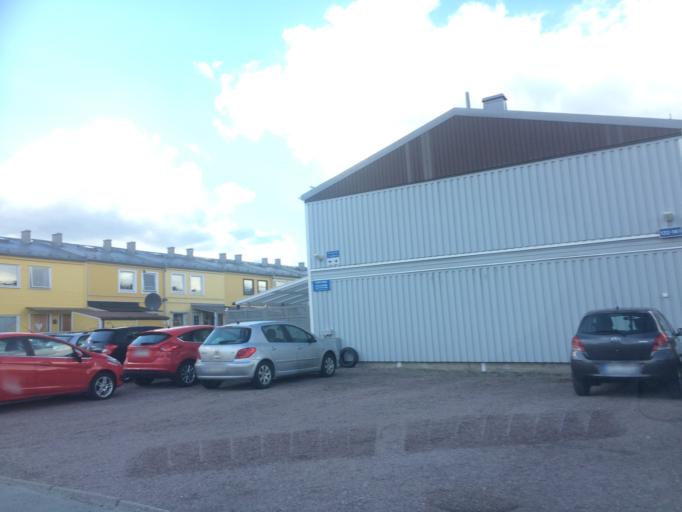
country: SE
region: Vaestra Goetaland
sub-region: Goteborg
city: Gardsten
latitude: 57.7923
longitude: 11.9972
